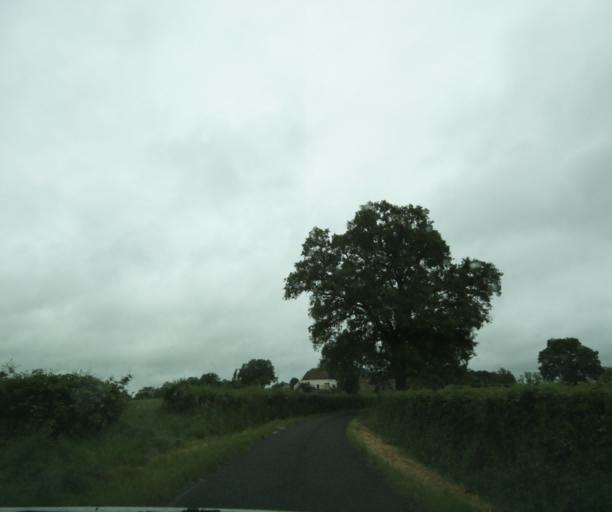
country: FR
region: Bourgogne
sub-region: Departement de Saone-et-Loire
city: Palinges
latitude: 46.5495
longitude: 4.1971
